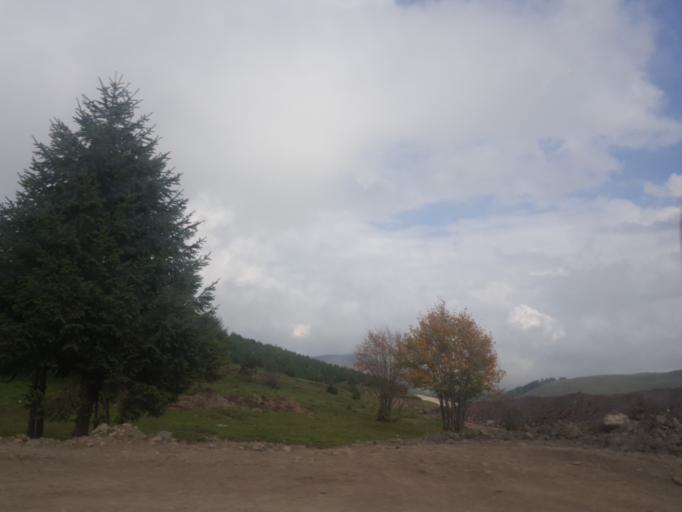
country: TR
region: Tokat
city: Bereketli
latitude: 40.5833
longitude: 37.3021
